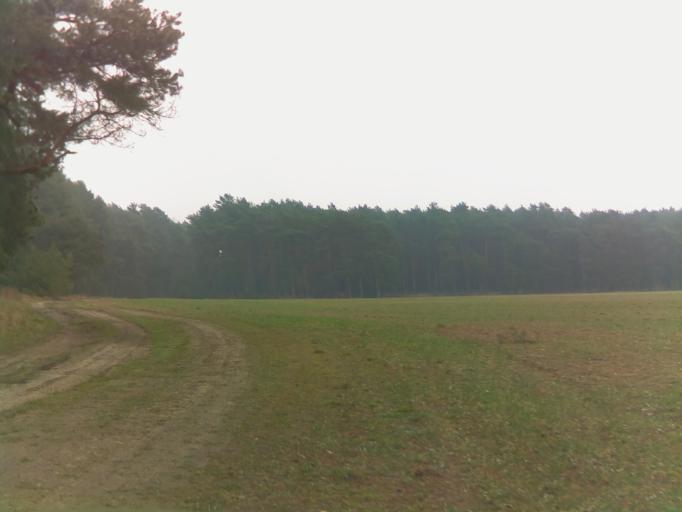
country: DE
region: Brandenburg
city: Neu Zauche
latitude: 51.9686
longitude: 14.1161
